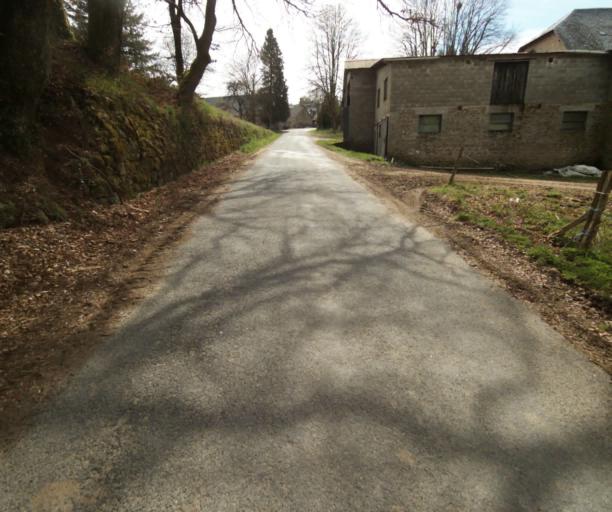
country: FR
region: Limousin
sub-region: Departement de la Correze
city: Correze
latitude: 45.3775
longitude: 1.9352
